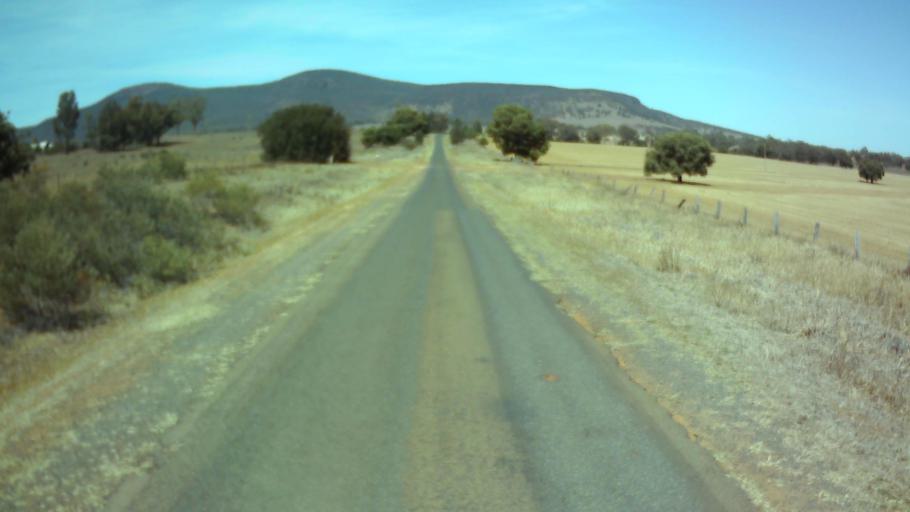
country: AU
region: New South Wales
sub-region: Weddin
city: Grenfell
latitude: -33.8625
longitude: 148.0129
